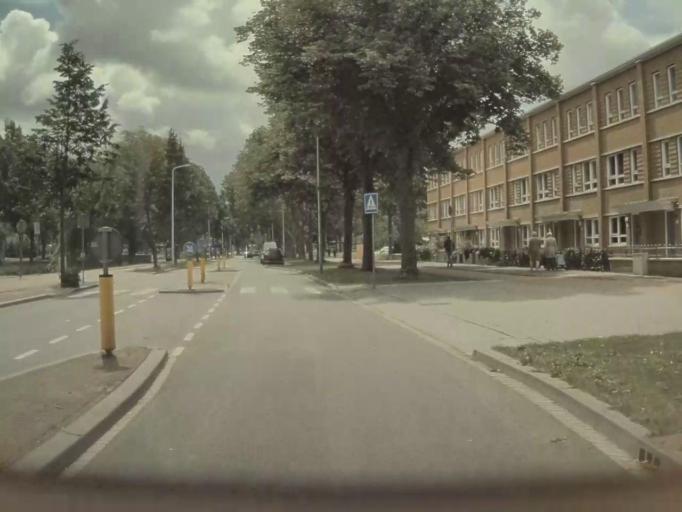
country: NL
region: South Holland
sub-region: Gemeente Westland
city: Kwintsheul
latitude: 52.0416
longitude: 4.2643
